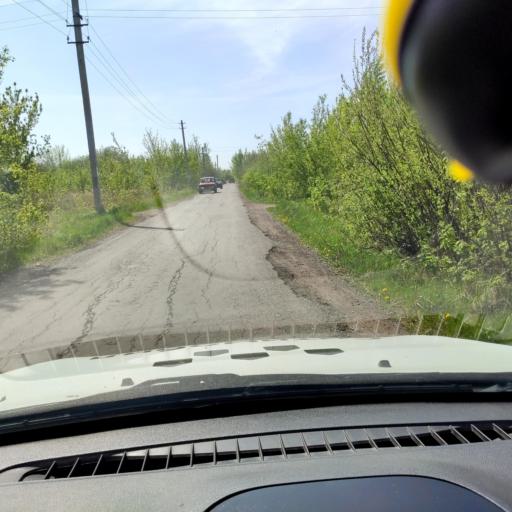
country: RU
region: Samara
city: Tol'yatti
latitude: 53.6656
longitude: 49.3626
